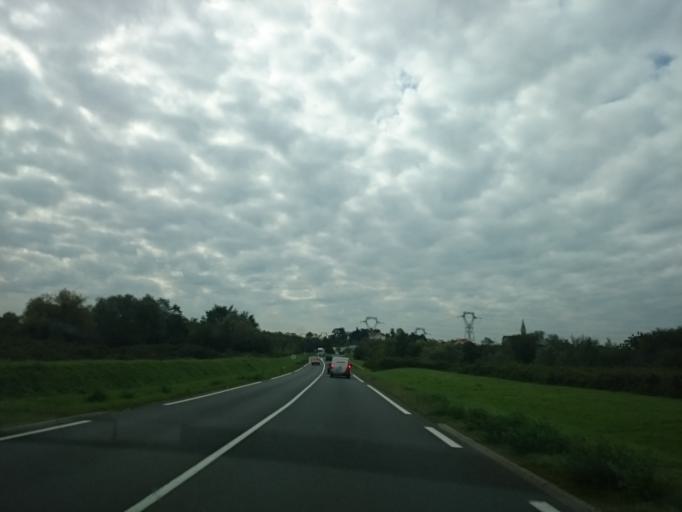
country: FR
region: Pays de la Loire
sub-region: Departement de la Loire-Atlantique
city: Indre
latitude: 47.2051
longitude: -1.6671
